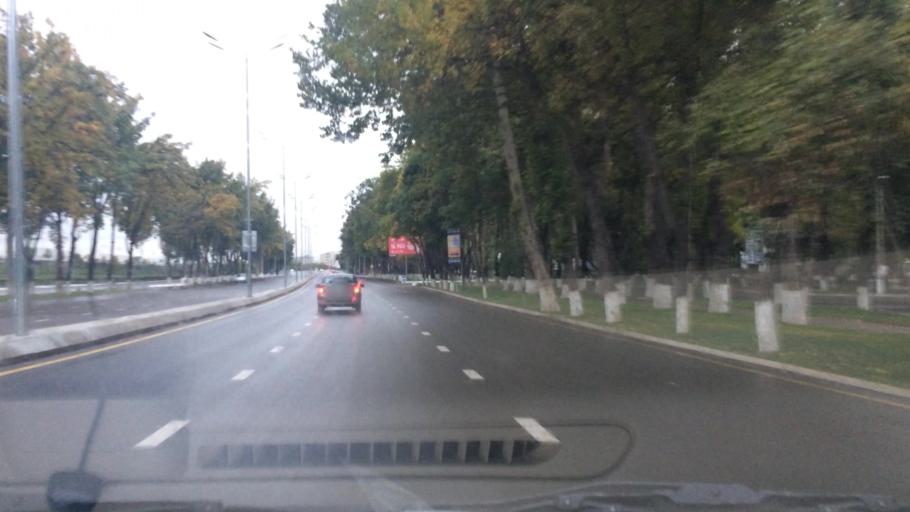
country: UZ
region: Toshkent Shahri
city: Tashkent
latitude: 41.2791
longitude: 69.2088
